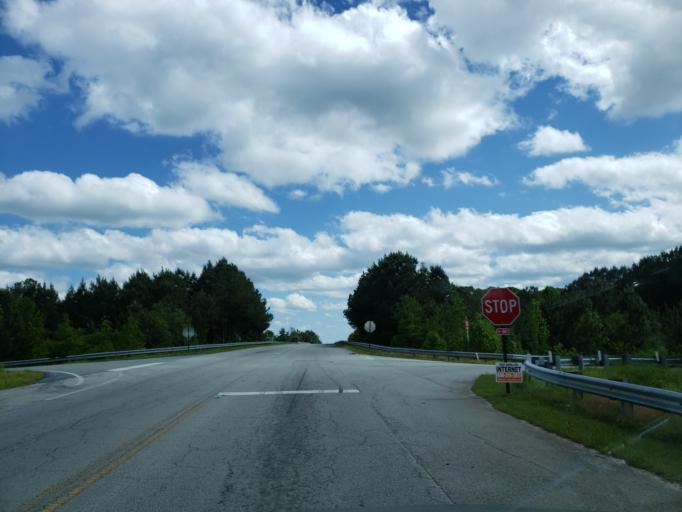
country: US
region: Georgia
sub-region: Haralson County
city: Bremen
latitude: 33.7319
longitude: -85.1122
